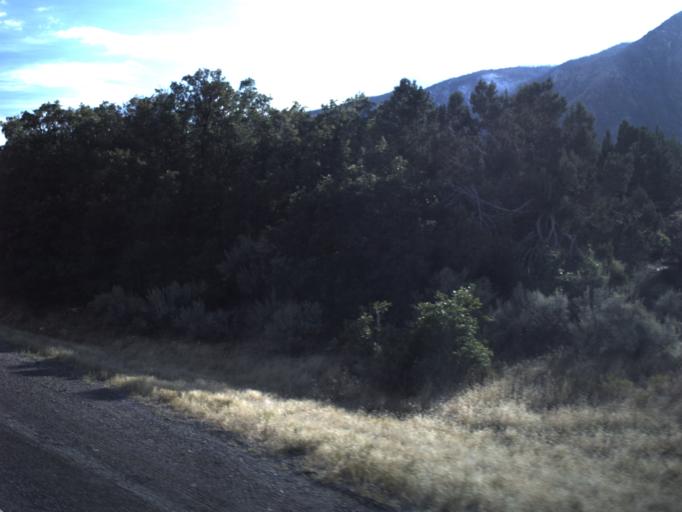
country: US
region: Utah
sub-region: Sanpete County
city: Gunnison
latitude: 39.1759
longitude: -112.0761
